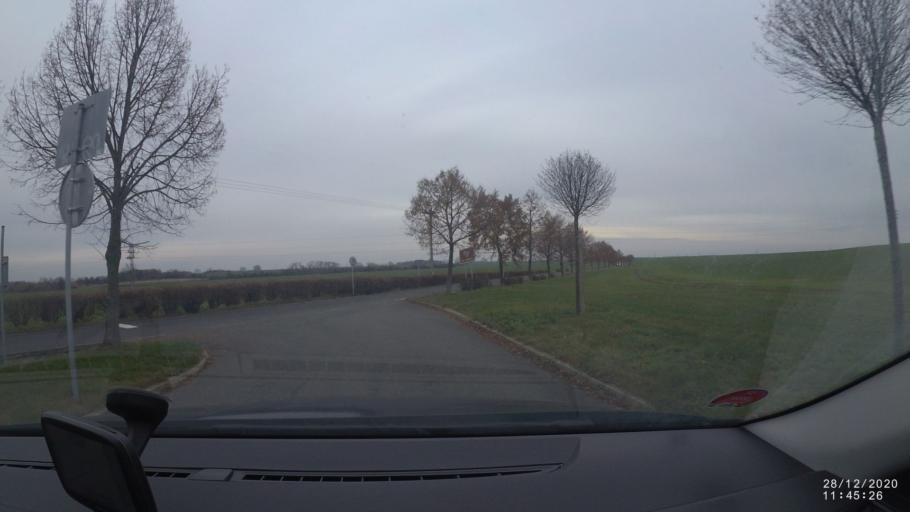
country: CZ
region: Central Bohemia
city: Zelenec
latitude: 50.1336
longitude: 14.6662
